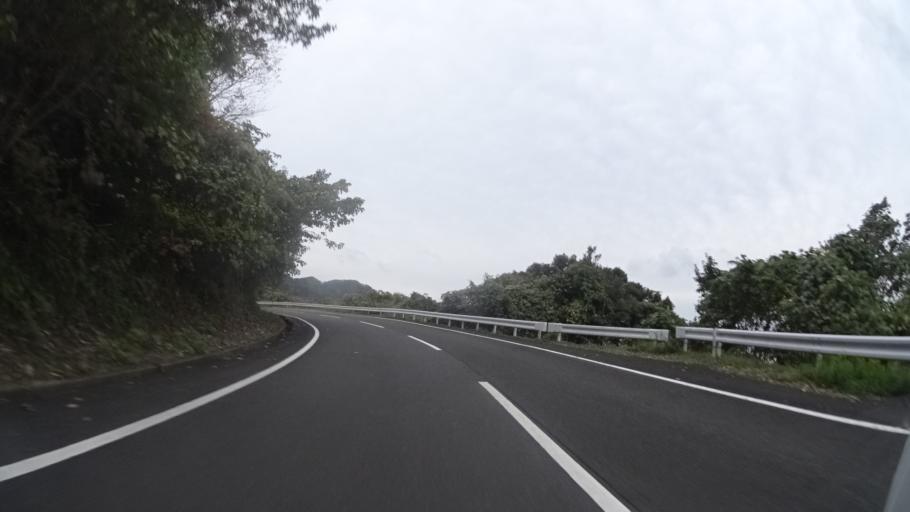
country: JP
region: Kyoto
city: Maizuru
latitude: 35.5711
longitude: 135.4497
